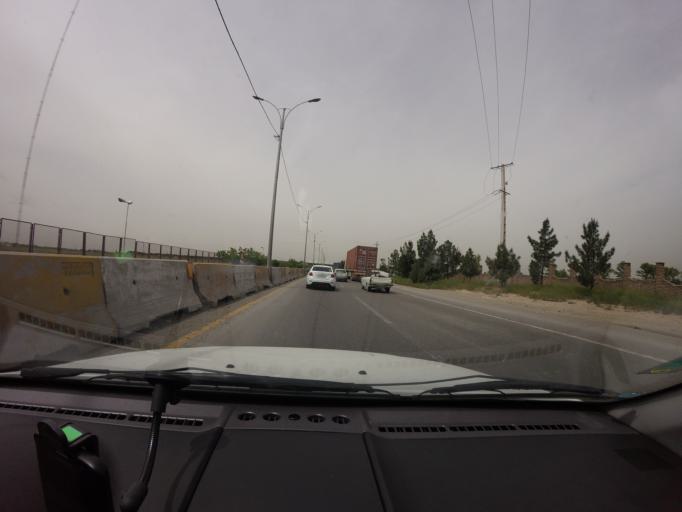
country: IR
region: Tehran
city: Eslamshahr
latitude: 35.5947
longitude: 51.2459
